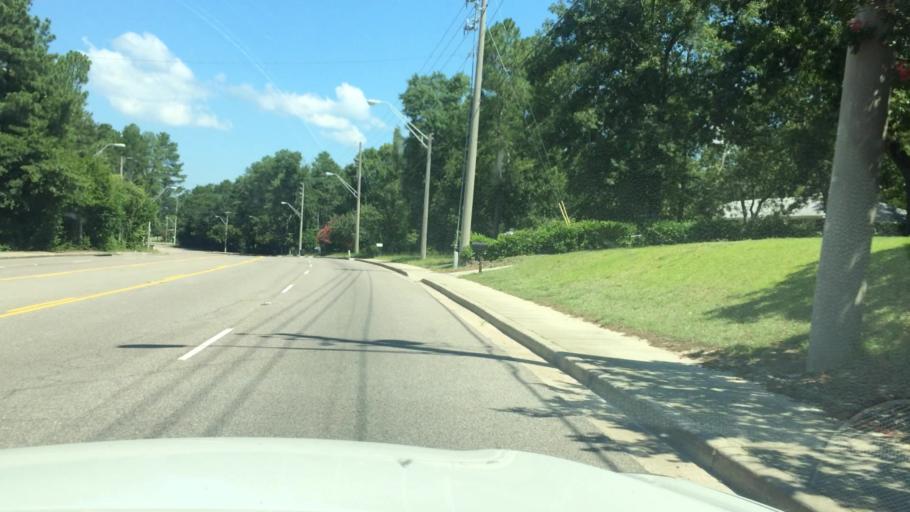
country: US
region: South Carolina
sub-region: Aiken County
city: North Augusta
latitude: 33.5271
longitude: -81.9795
